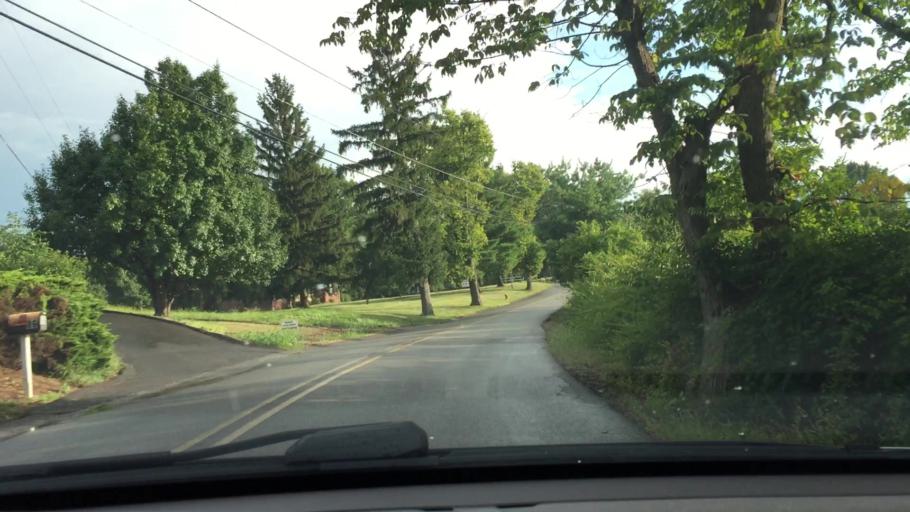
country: US
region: Pennsylvania
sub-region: Washington County
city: McGovern
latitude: 40.2139
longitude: -80.1847
